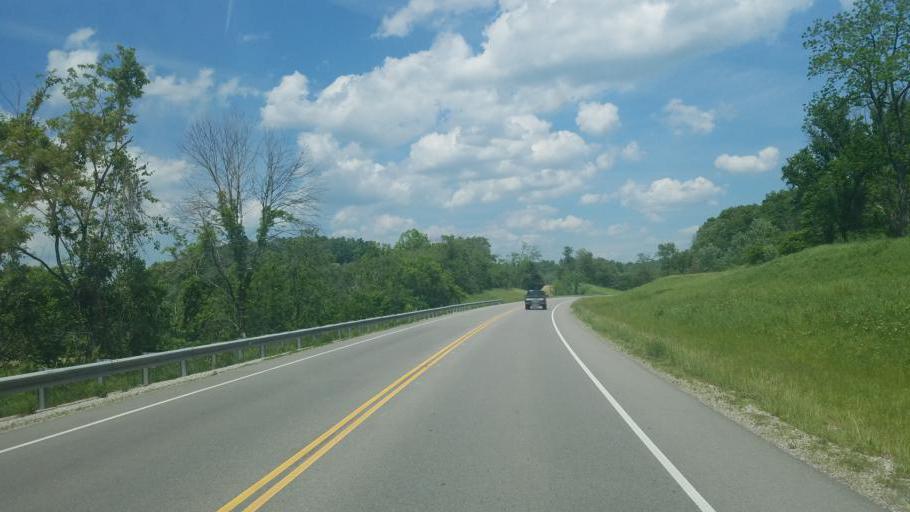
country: US
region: Ohio
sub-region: Meigs County
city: Middleport
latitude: 39.0013
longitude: -82.0757
